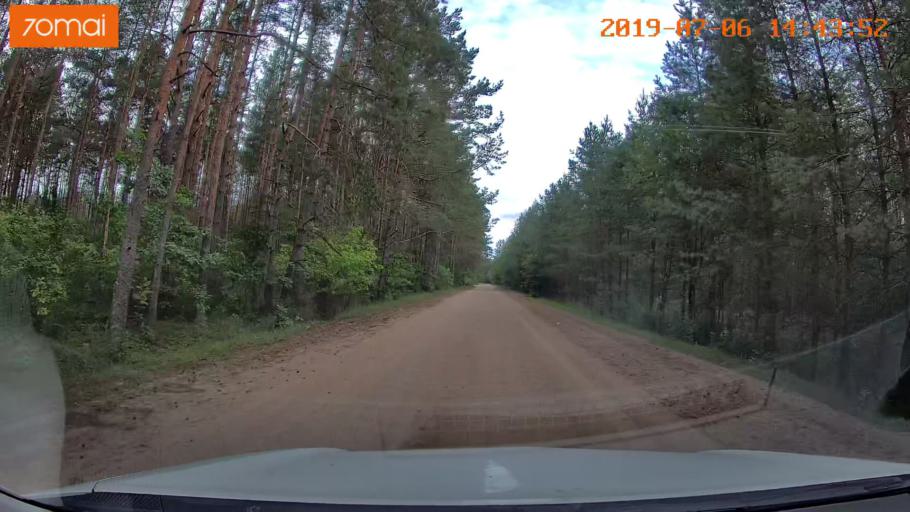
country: BY
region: Minsk
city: Ivyanyets
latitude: 53.9559
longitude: 26.6944
